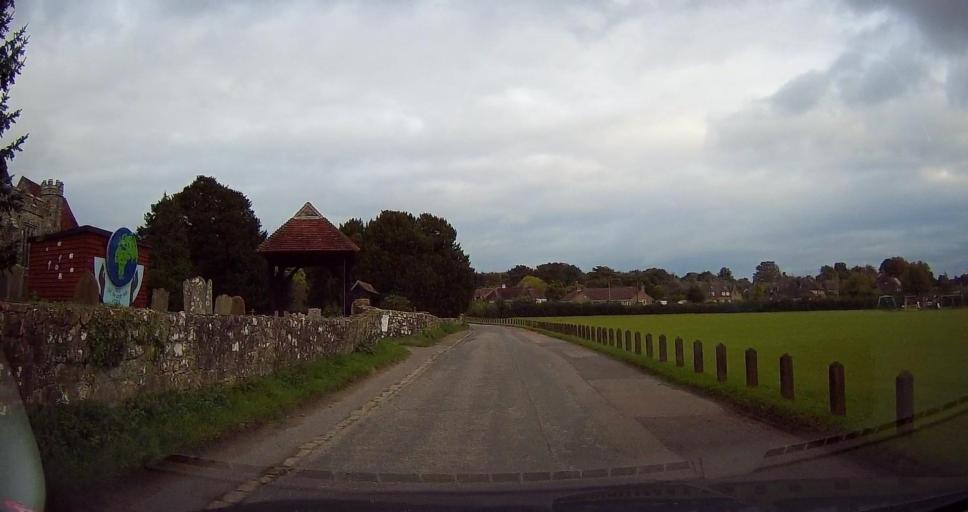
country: GB
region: England
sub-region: Kent
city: Harrietsham
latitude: 51.2452
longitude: 0.6844
